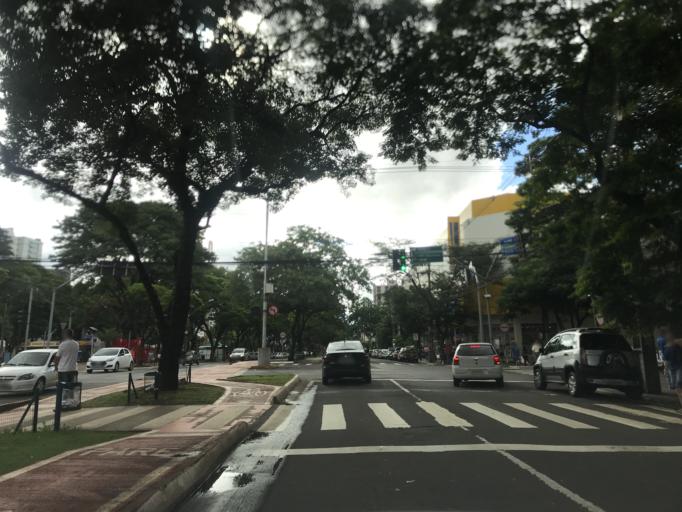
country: BR
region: Parana
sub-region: Maringa
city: Maringa
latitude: -23.4208
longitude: -51.9395
